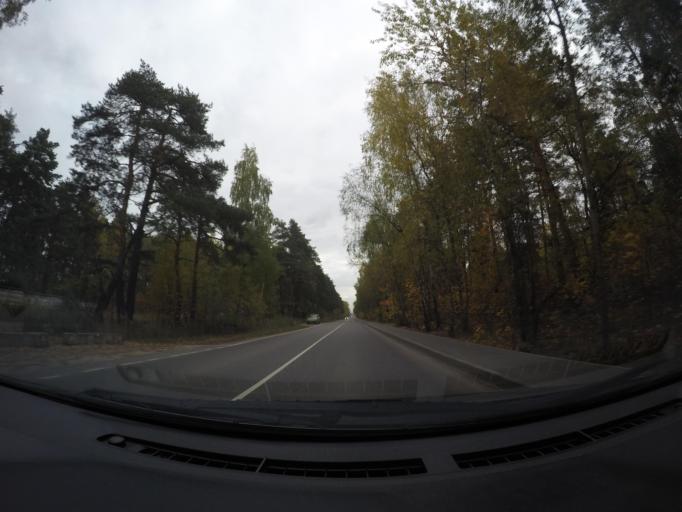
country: RU
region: Moskovskaya
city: Vishnyakovskiye Dachi
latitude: 55.8059
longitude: 38.1224
